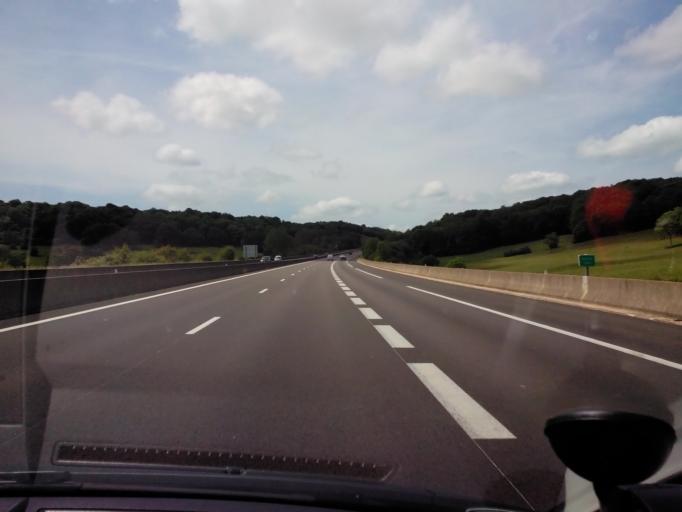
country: FR
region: Champagne-Ardenne
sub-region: Departement de la Haute-Marne
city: Rolampont
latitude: 47.9229
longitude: 5.2744
